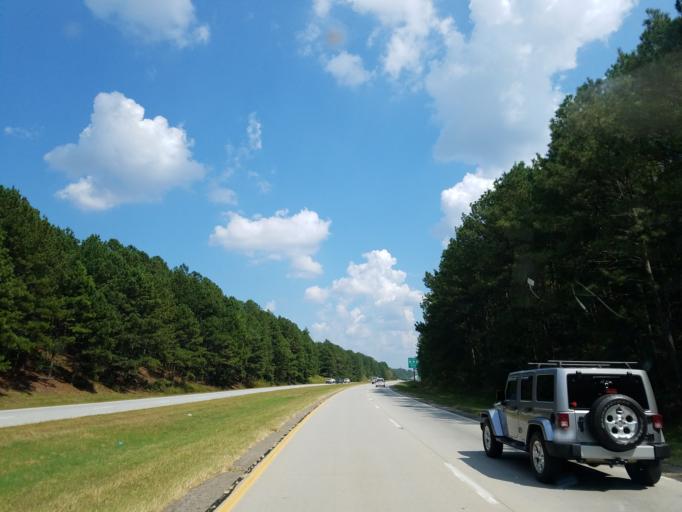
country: US
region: Georgia
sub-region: Oconee County
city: Watkinsville
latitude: 33.9155
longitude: -83.4237
